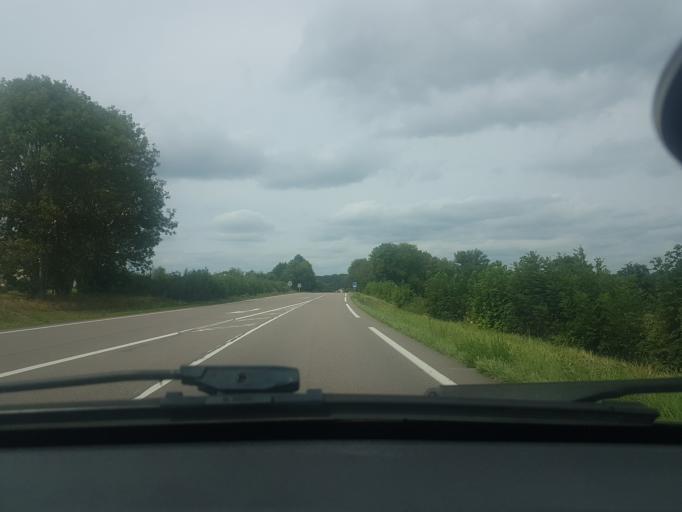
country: FR
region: Bourgogne
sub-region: Departement de la Cote-d'Or
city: Arnay-le-Duc
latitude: 47.0748
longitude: 4.5694
